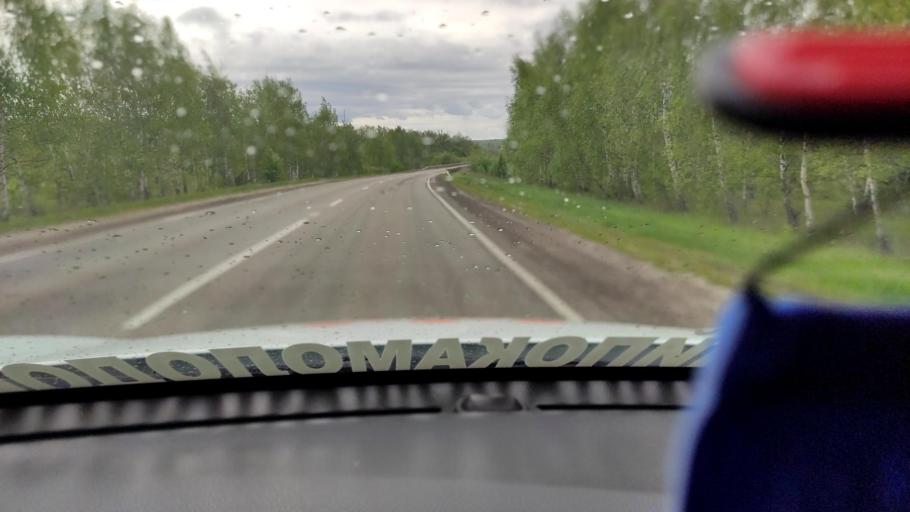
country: RU
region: Voronezj
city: Imeni Pervogo Maya
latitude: 50.7631
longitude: 39.3899
